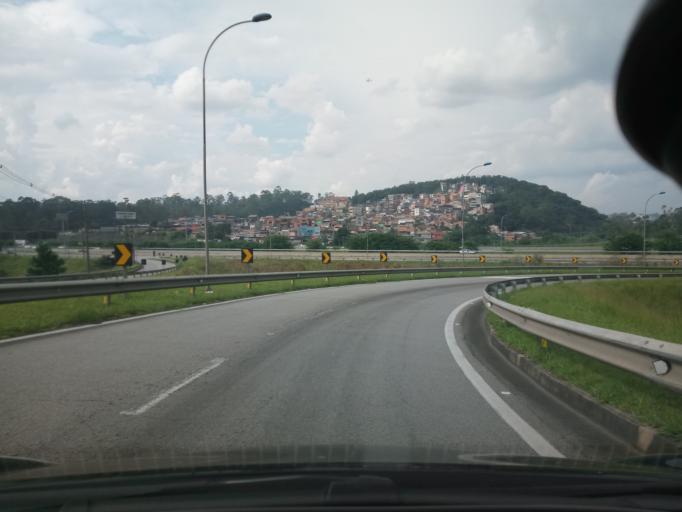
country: BR
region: Sao Paulo
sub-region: Sao Bernardo Do Campo
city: Sao Bernardo do Campo
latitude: -23.7561
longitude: -46.5950
